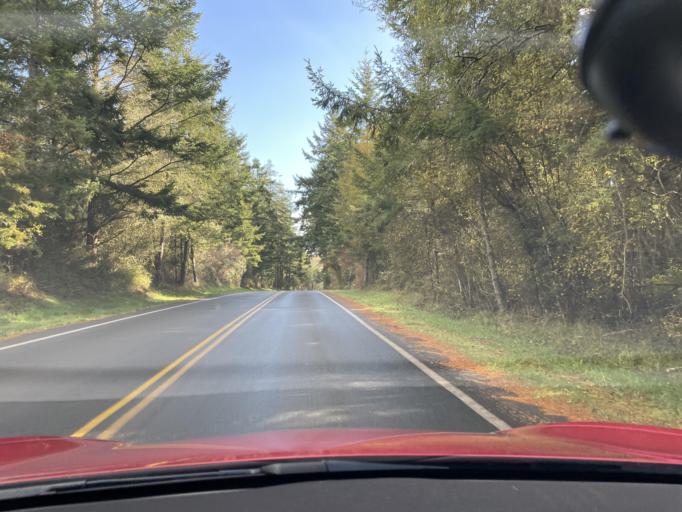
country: US
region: Washington
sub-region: San Juan County
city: Friday Harbor
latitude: 48.4692
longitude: -123.0189
